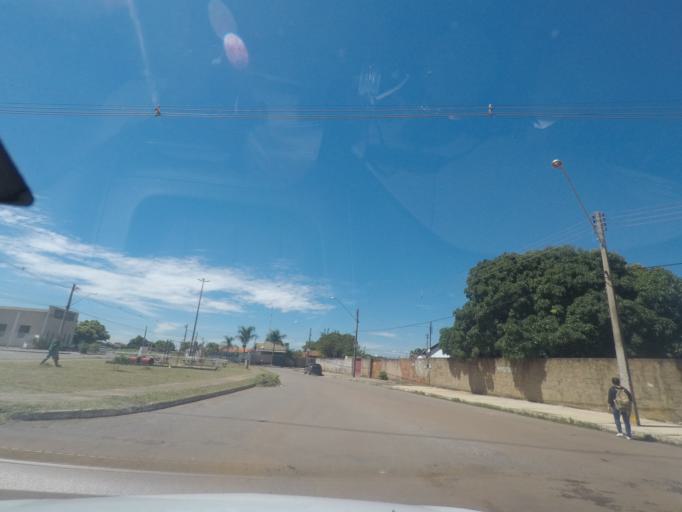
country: BR
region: Goias
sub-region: Aparecida De Goiania
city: Aparecida de Goiania
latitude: -16.7830
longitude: -49.3339
